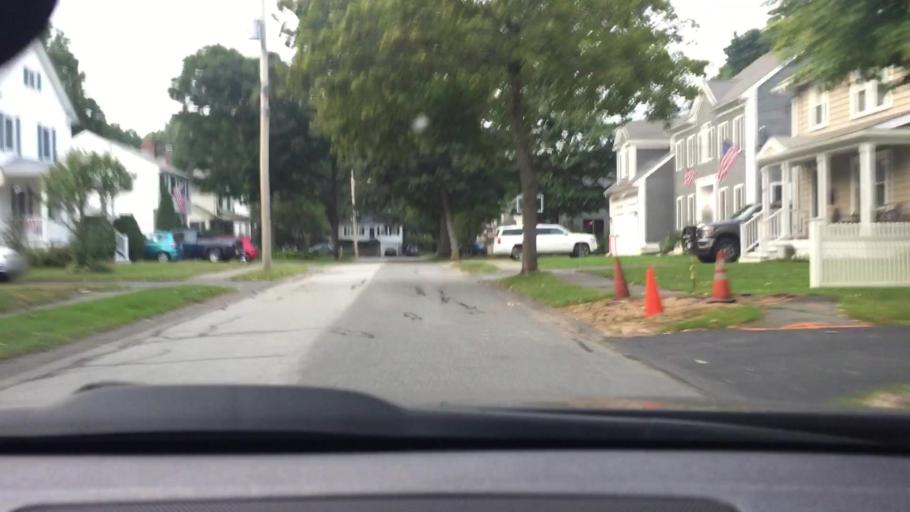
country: US
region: Massachusetts
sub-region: Norfolk County
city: Needham
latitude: 42.2823
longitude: -71.2249
